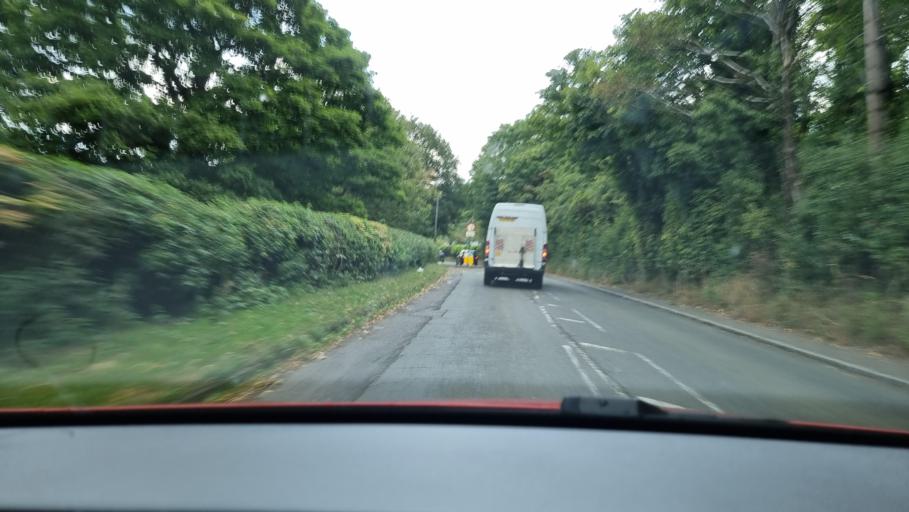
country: GB
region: England
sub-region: Buckinghamshire
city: Ivinghoe
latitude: 51.8349
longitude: -0.6264
